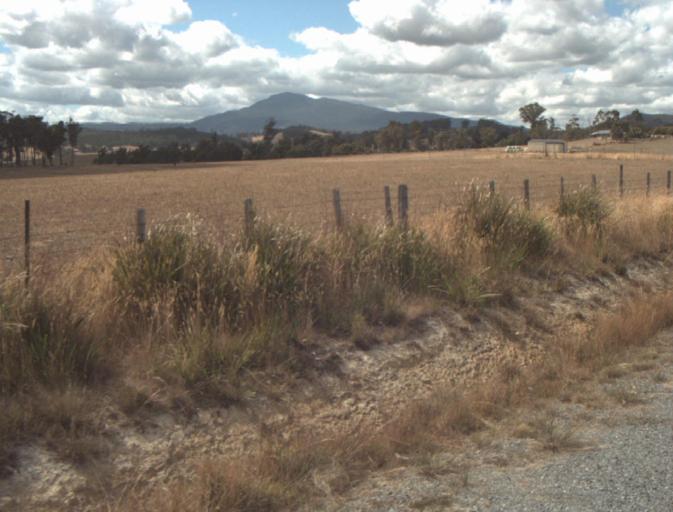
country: AU
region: Tasmania
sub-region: Launceston
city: Mayfield
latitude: -41.2125
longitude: 147.1343
